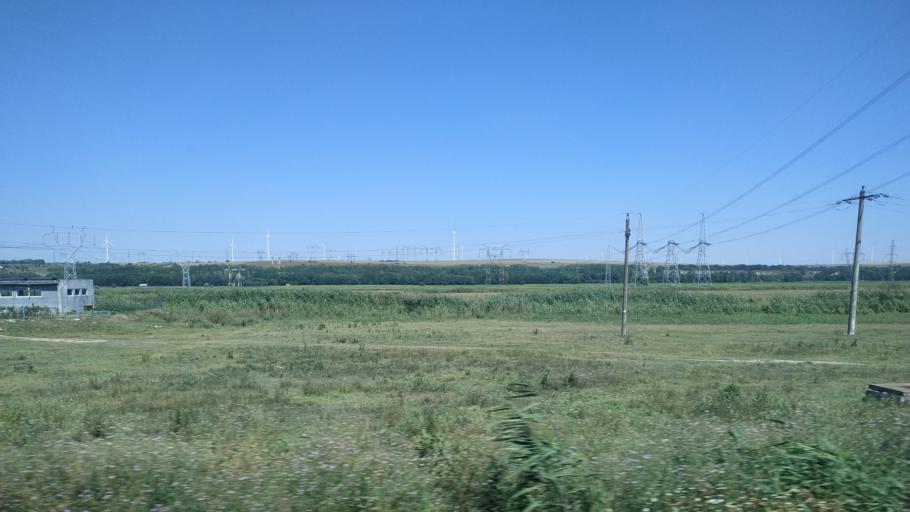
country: RO
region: Constanta
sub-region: Comuna Saligny
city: Faclia
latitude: 44.2697
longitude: 28.1216
